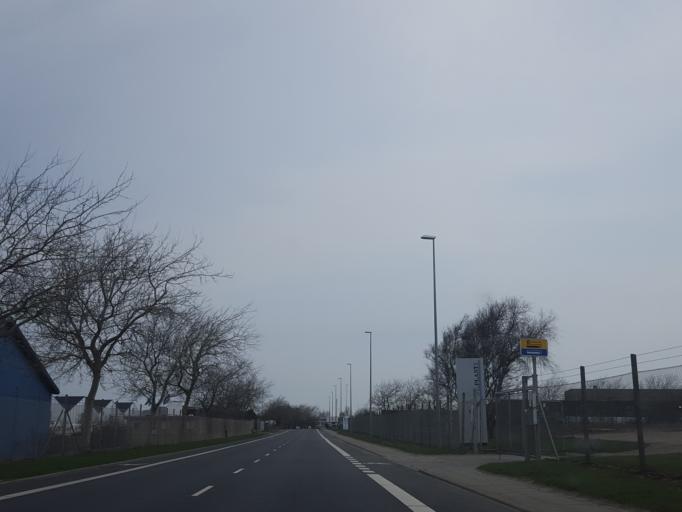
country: DK
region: South Denmark
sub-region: Esbjerg Kommune
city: Esbjerg
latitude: 55.4889
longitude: 8.4658
